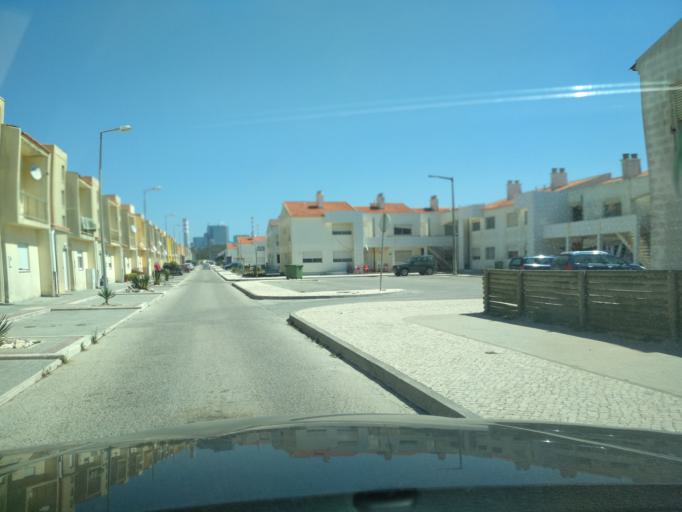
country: PT
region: Coimbra
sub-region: Figueira da Foz
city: Lavos
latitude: 40.0550
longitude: -8.8901
